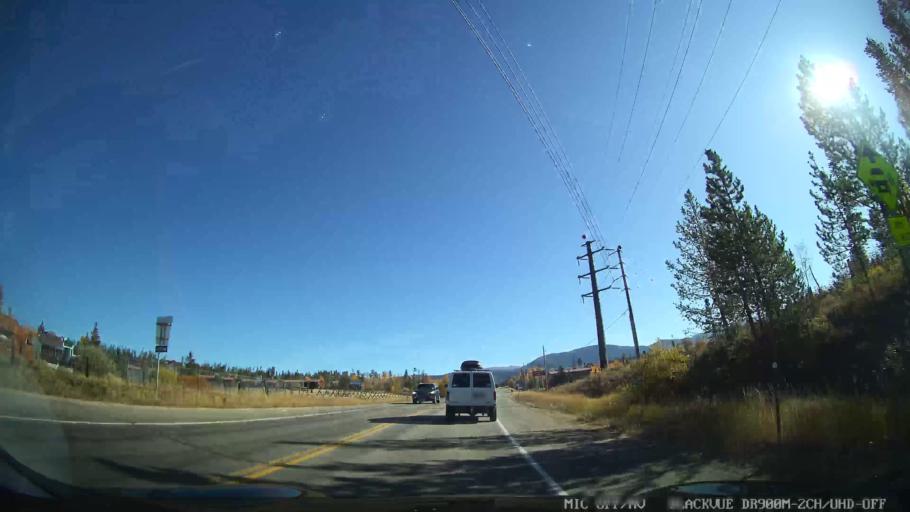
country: US
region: Colorado
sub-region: Grand County
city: Granby
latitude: 40.1948
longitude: -105.8772
